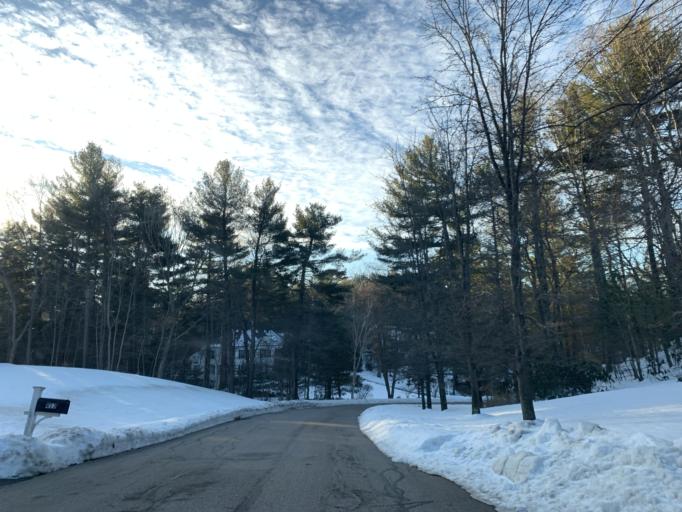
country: US
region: Massachusetts
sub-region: Norfolk County
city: Westwood
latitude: 42.2456
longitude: -71.2305
